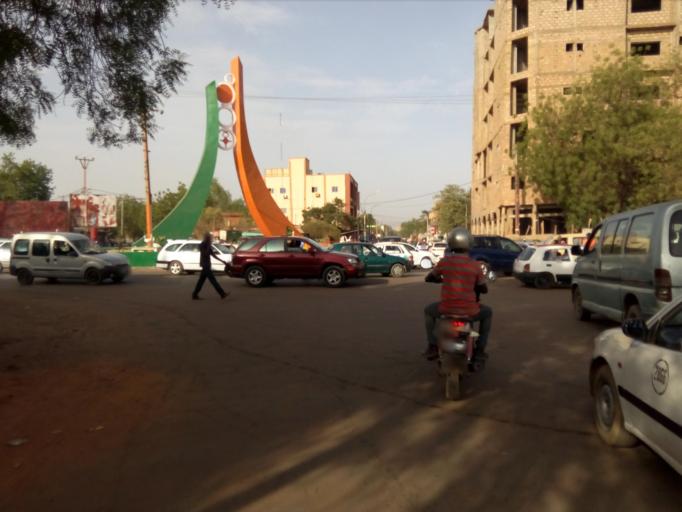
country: NE
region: Niamey
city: Niamey
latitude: 13.5112
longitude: 2.1212
